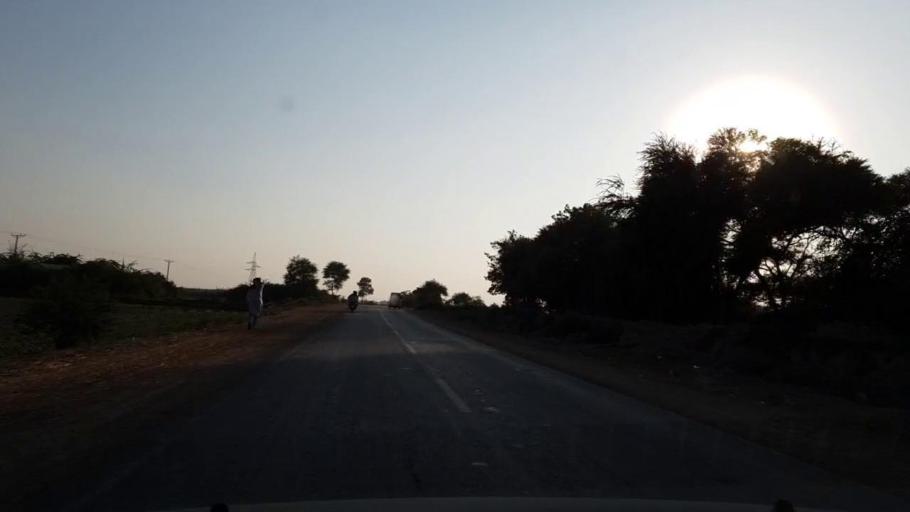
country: PK
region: Sindh
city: Daro Mehar
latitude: 24.6548
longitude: 68.1292
